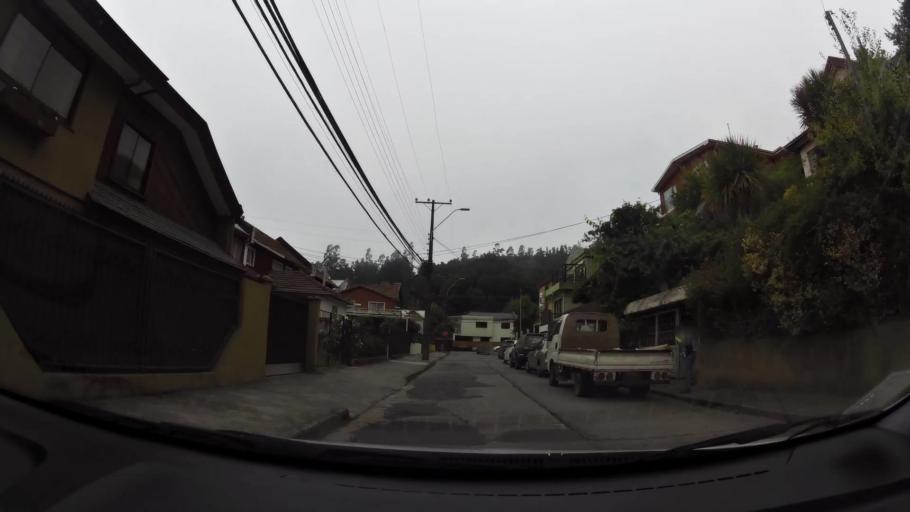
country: CL
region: Biobio
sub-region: Provincia de Concepcion
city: Concepcion
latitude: -36.8218
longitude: -73.0331
